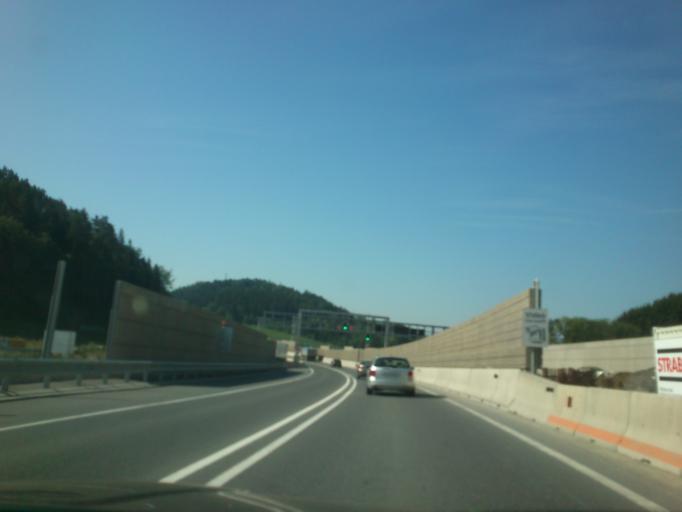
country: AT
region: Upper Austria
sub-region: Politischer Bezirk Freistadt
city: Freistadt
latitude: 48.4404
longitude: 14.4808
